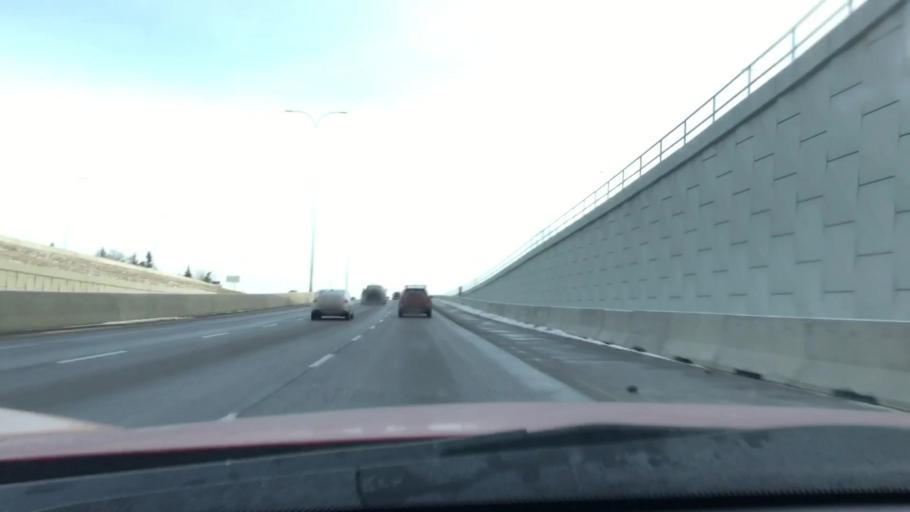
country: CA
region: Alberta
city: Calgary
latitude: 51.0830
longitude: -114.2086
